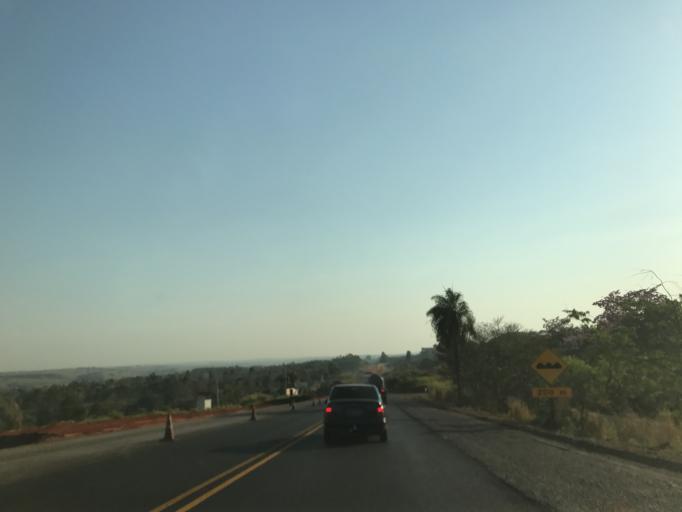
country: BR
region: Sao Paulo
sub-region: Marilia
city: Marilia
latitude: -22.1210
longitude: -49.9318
